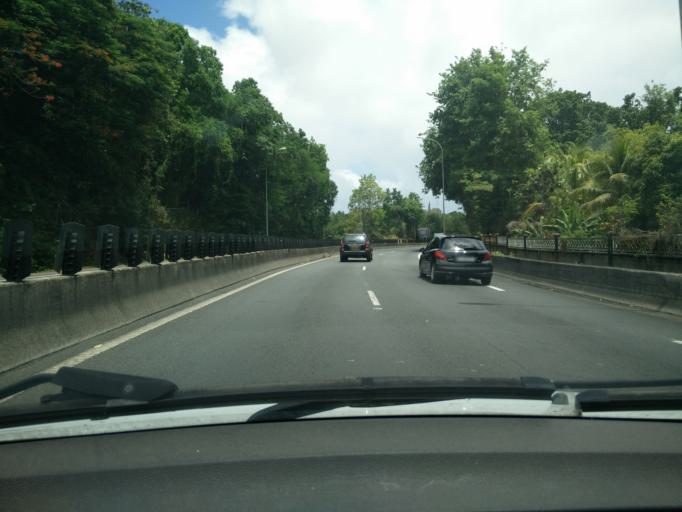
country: GP
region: Guadeloupe
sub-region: Guadeloupe
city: Pointe-a-Pitre
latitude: 16.2428
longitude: -61.5227
